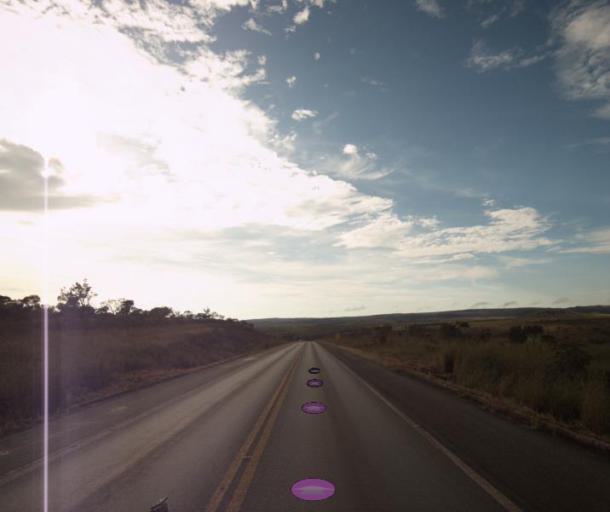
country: BR
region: Goias
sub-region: Pirenopolis
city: Pirenopolis
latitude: -15.7670
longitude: -48.7220
